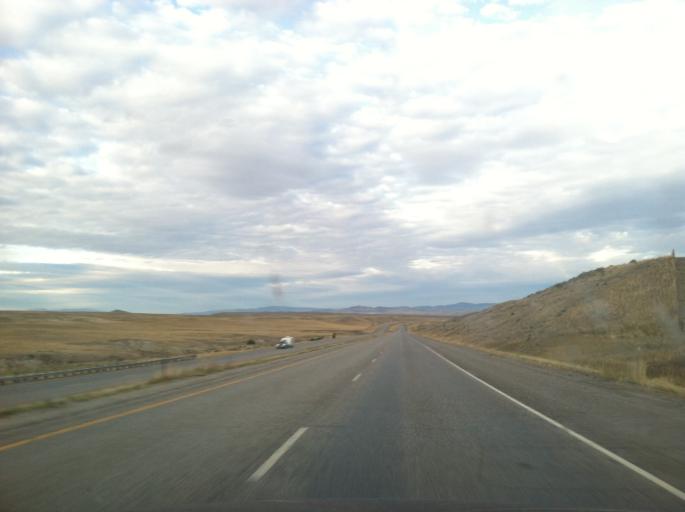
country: US
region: Montana
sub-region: Gallatin County
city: Three Forks
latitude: 45.9035
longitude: -111.8075
